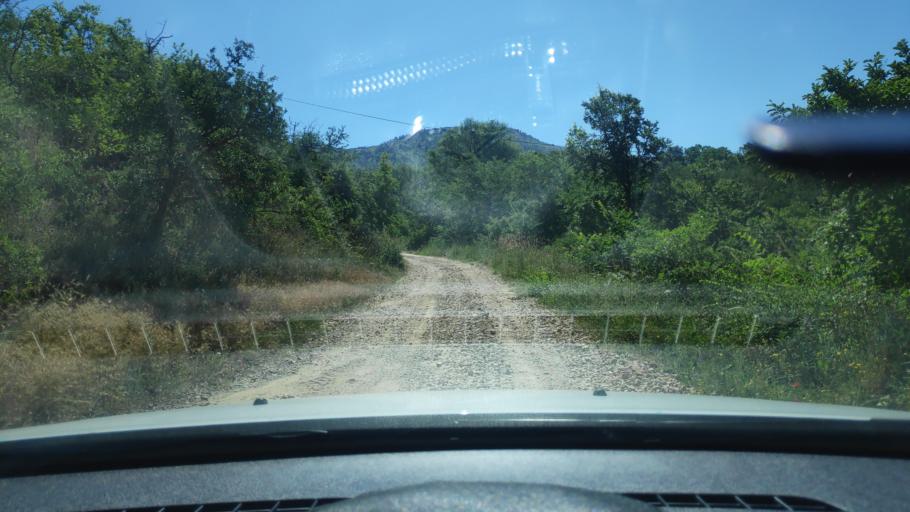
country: MK
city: Klechovce
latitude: 42.0727
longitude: 21.8969
